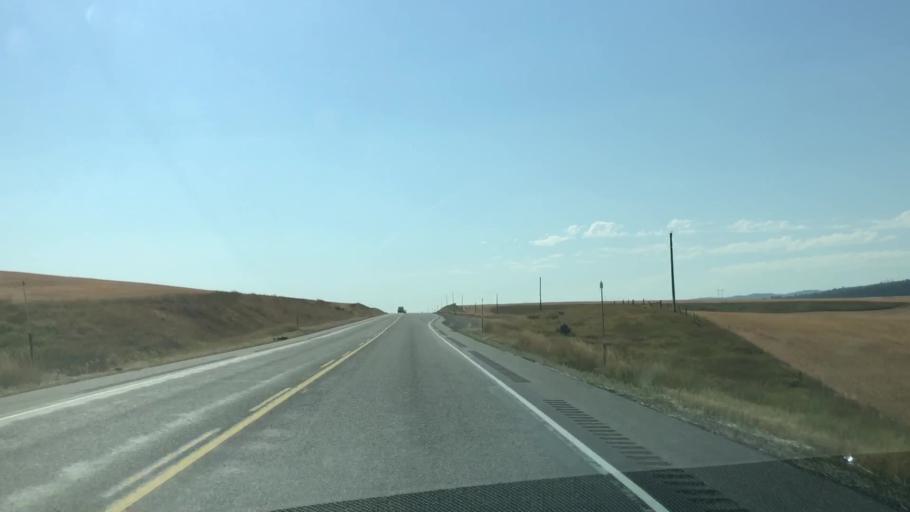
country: US
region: Idaho
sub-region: Teton County
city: Victor
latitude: 43.5330
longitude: -111.5075
